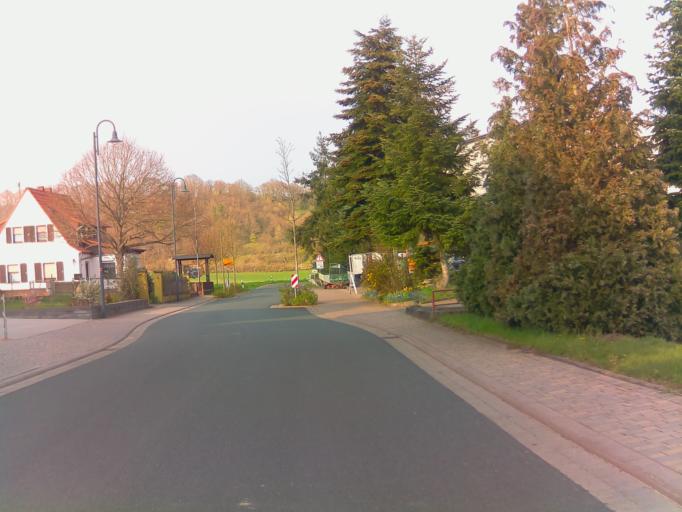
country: DE
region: Rheinland-Pfalz
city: Sponheim
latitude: 49.8454
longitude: 7.7294
